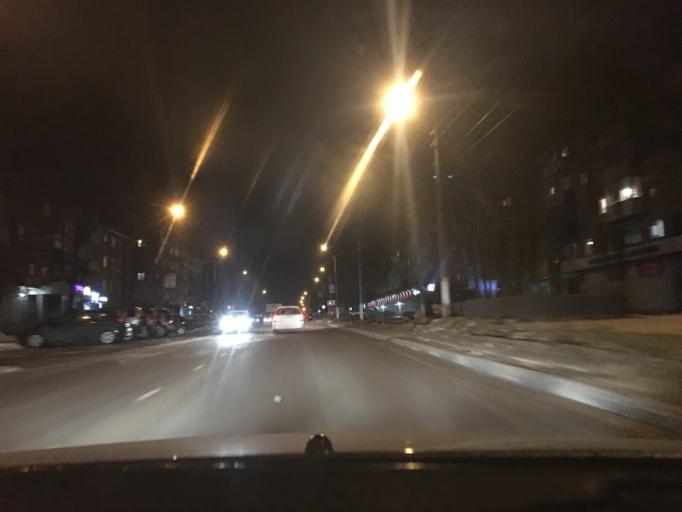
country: RU
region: Tula
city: Shchekino
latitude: 54.0182
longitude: 37.5061
